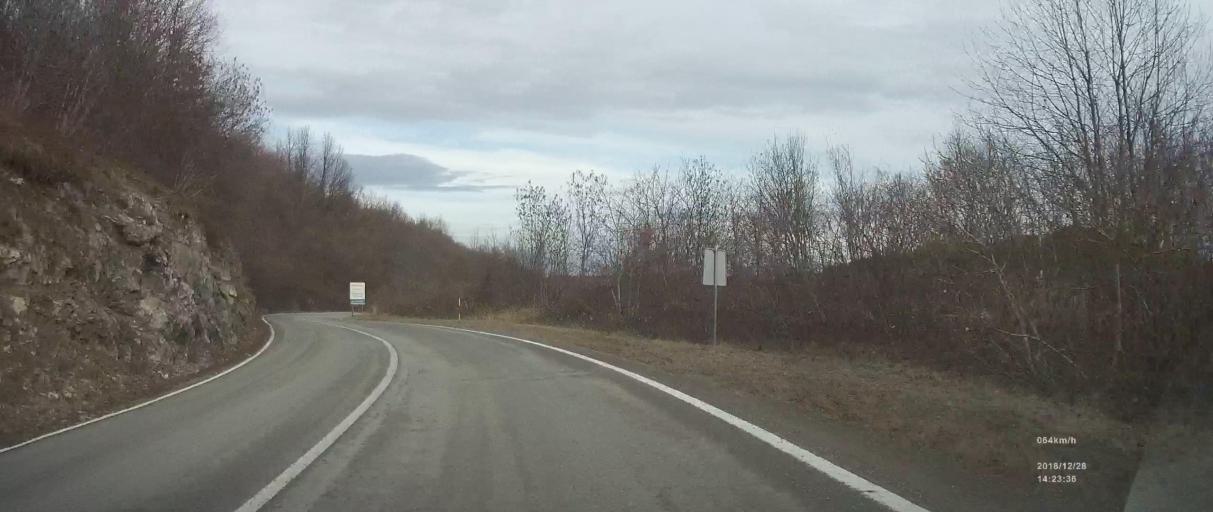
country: HR
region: Primorsko-Goranska
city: Vrbovsko
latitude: 45.3810
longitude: 15.0974
